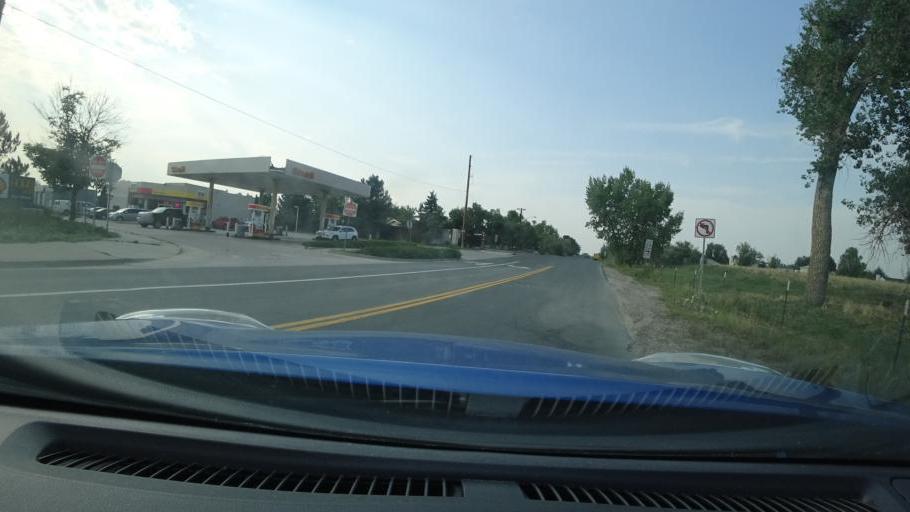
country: US
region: Colorado
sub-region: Adams County
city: Aurora
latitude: 39.7404
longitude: -104.7630
